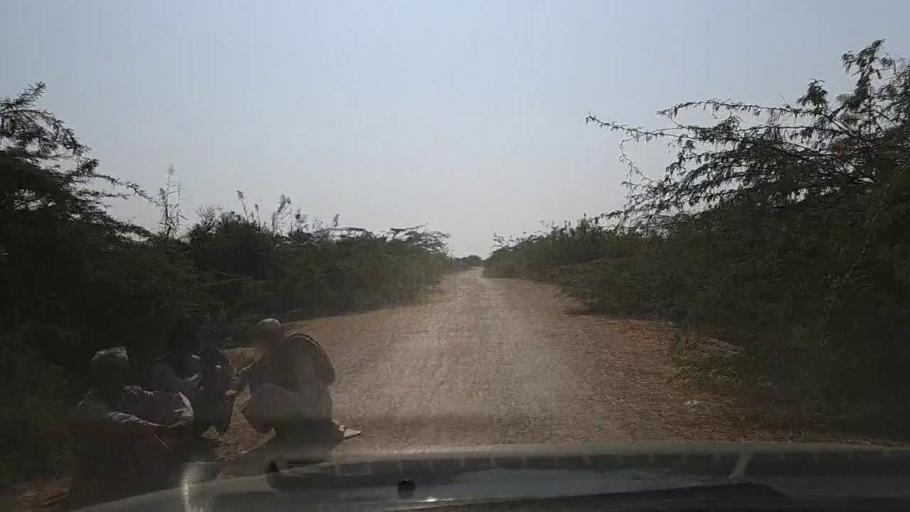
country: PK
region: Sindh
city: Mirpur Sakro
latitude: 24.3941
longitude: 67.6656
